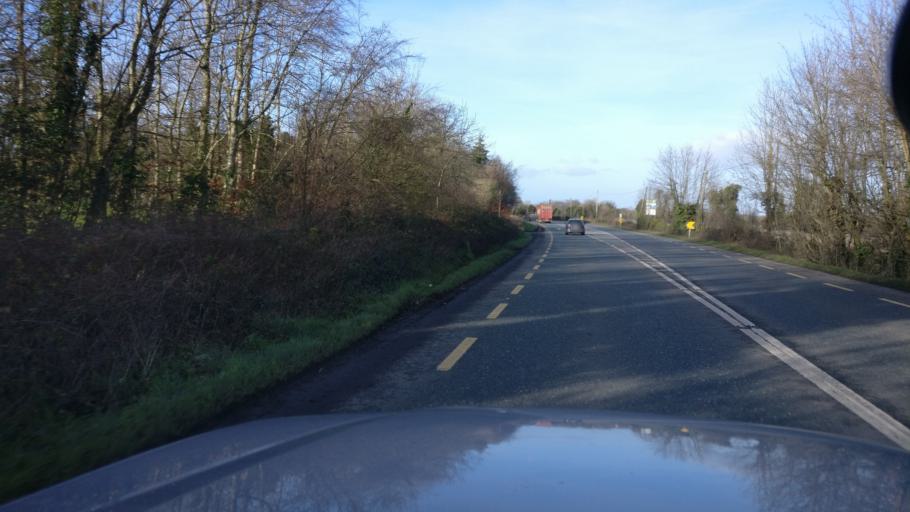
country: IE
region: Leinster
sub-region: Uibh Fhaili
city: Tullamore
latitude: 53.2301
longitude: -7.4754
